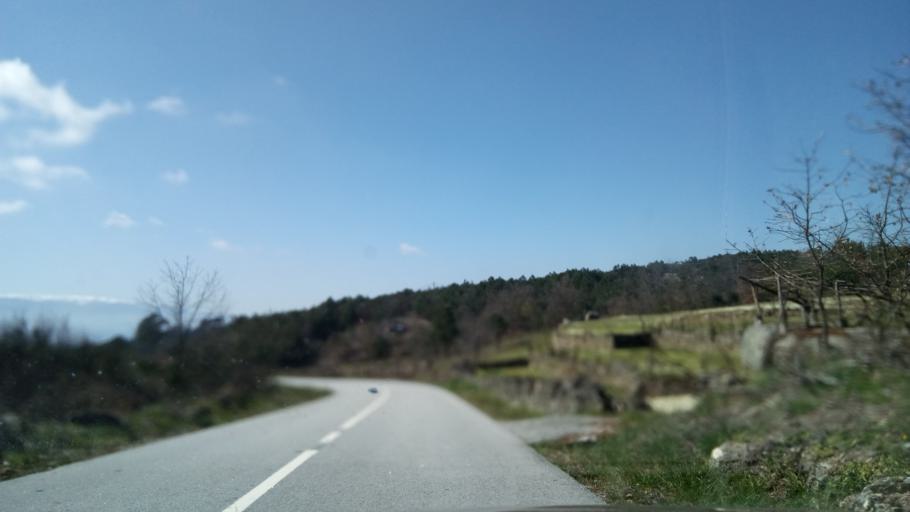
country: PT
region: Guarda
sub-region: Fornos de Algodres
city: Fornos de Algodres
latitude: 40.6387
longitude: -7.5327
